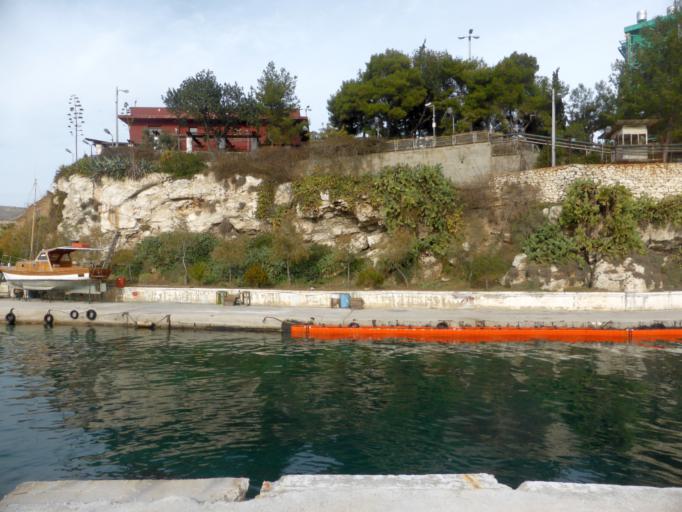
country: GR
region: Attica
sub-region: Nomos Piraios
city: Drapetsona
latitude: 37.9529
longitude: 23.6094
